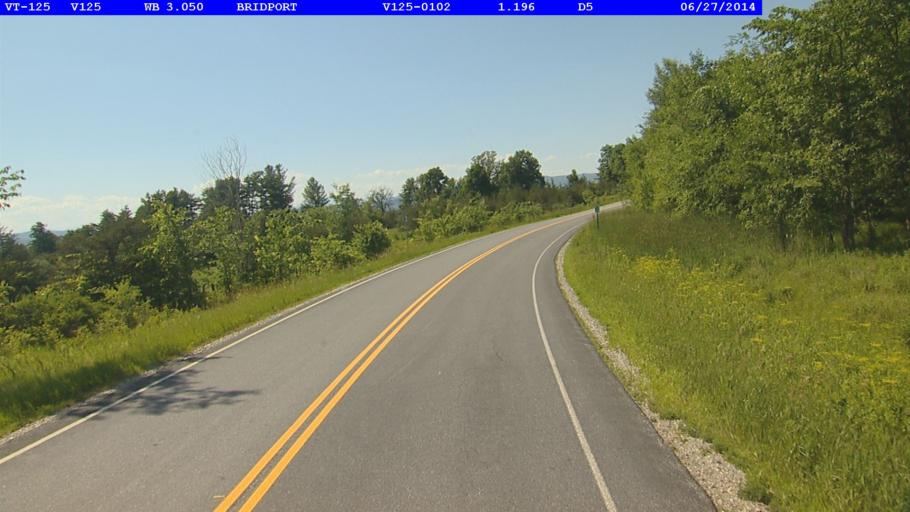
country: US
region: New York
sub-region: Essex County
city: Port Henry
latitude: 44.0053
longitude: -73.3840
